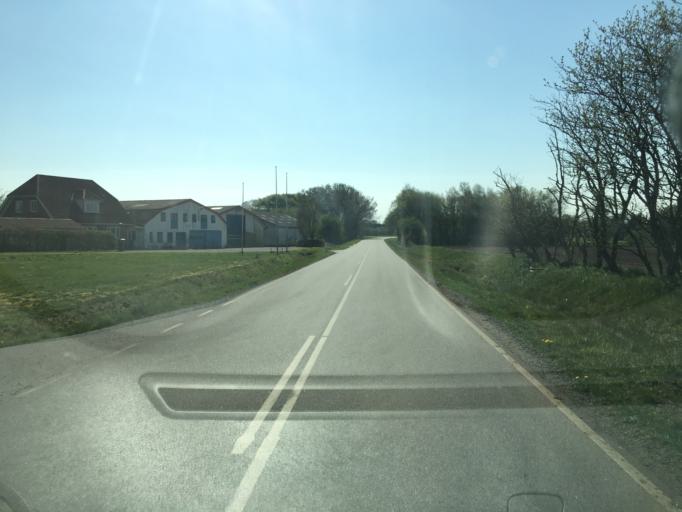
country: DK
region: South Denmark
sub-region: Haderslev Kommune
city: Vojens
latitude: 55.2816
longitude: 9.2056
